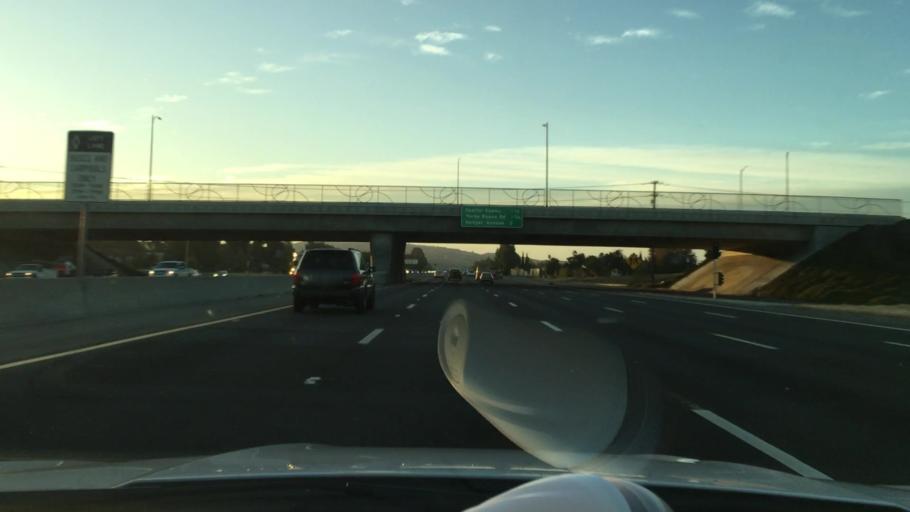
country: US
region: California
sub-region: Santa Clara County
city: Seven Trees
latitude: 37.3192
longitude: -121.8324
